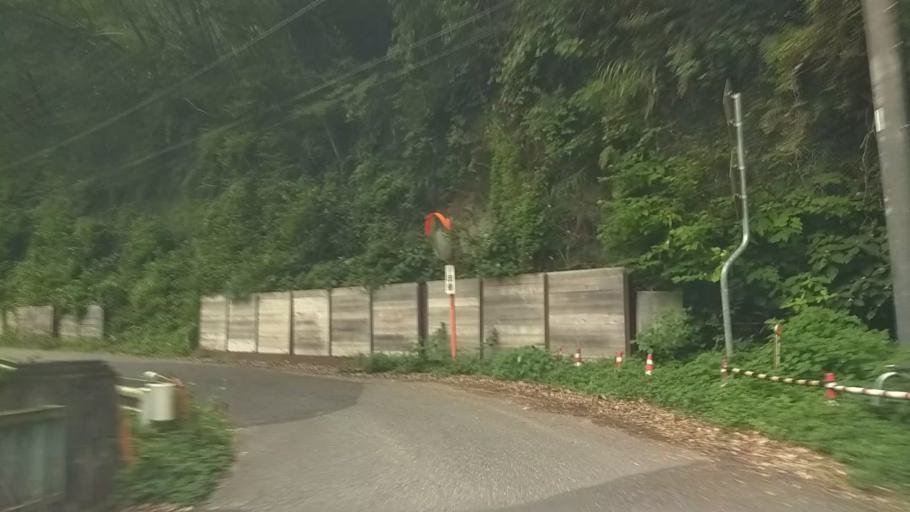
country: JP
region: Chiba
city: Kawaguchi
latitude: 35.1900
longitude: 140.1403
